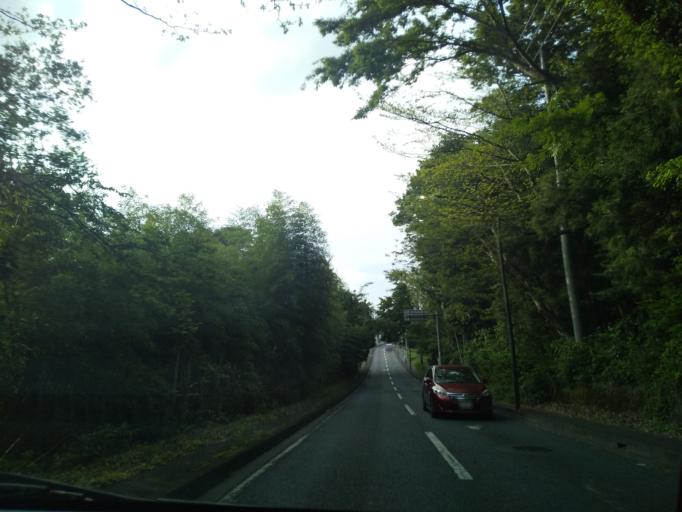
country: JP
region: Kanagawa
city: Zama
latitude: 35.5191
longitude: 139.3852
